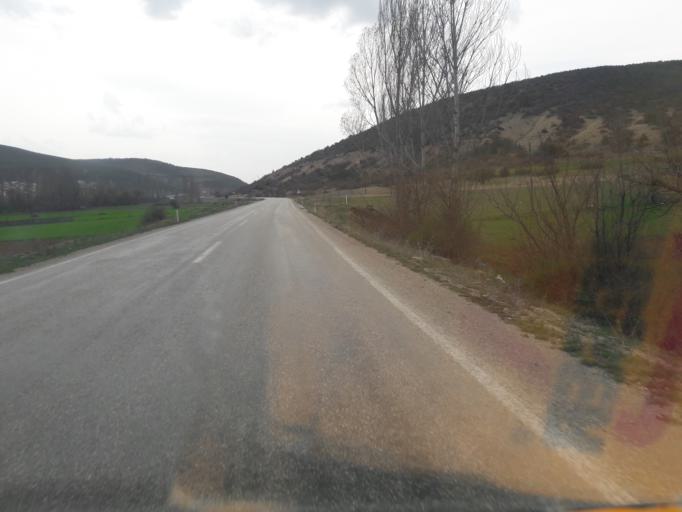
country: TR
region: Gumushane
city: Siran
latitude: 40.1771
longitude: 39.1441
